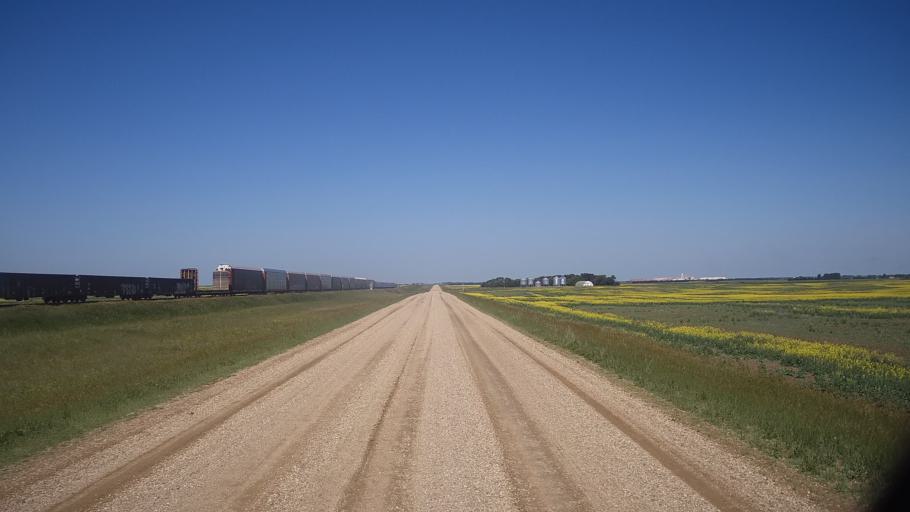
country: CA
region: Saskatchewan
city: Watrous
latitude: 51.8602
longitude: -105.9624
